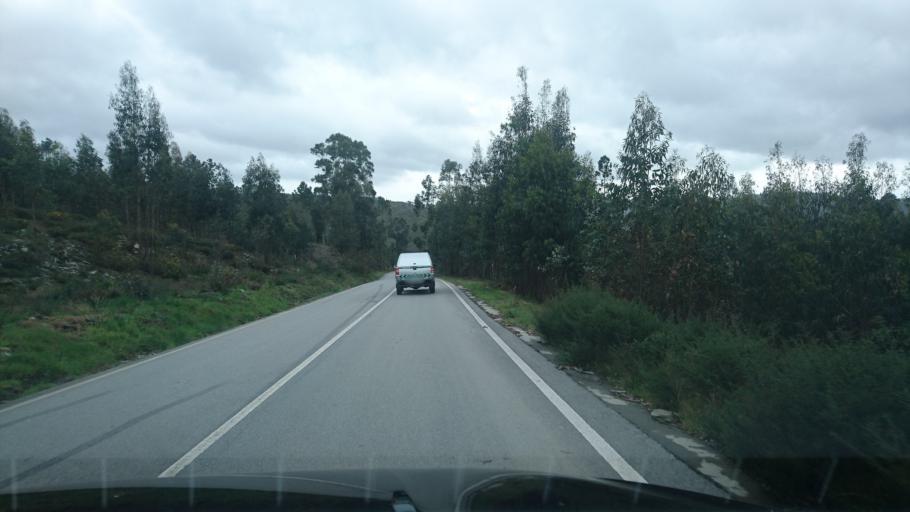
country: PT
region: Porto
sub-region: Paredes
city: Recarei
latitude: 41.1357
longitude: -8.4022
